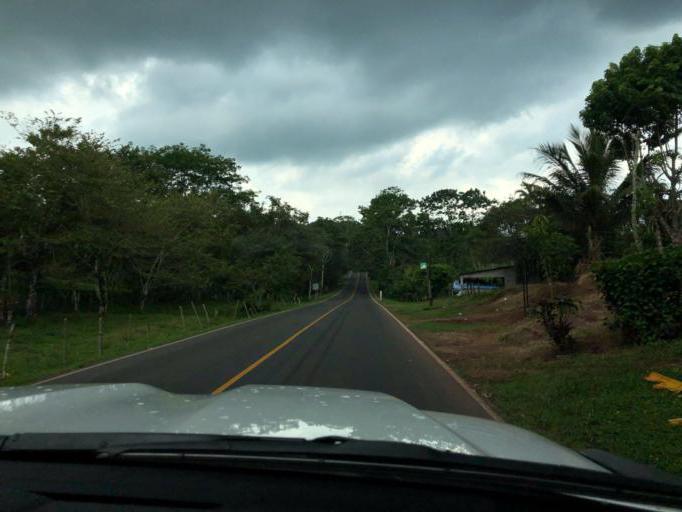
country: NI
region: Chontales
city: Villa Sandino
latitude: 11.9906
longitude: -84.8238
